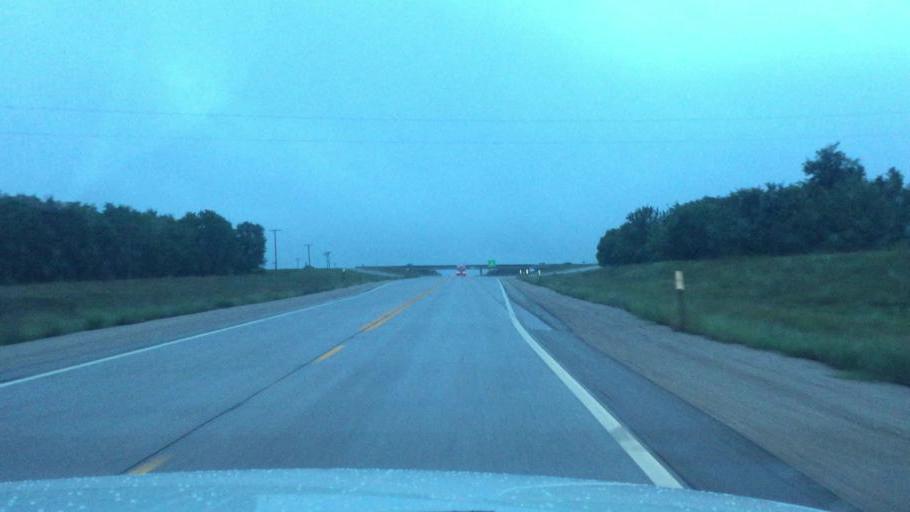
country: US
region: Kansas
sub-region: Allen County
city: Humboldt
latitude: 37.7959
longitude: -95.4114
